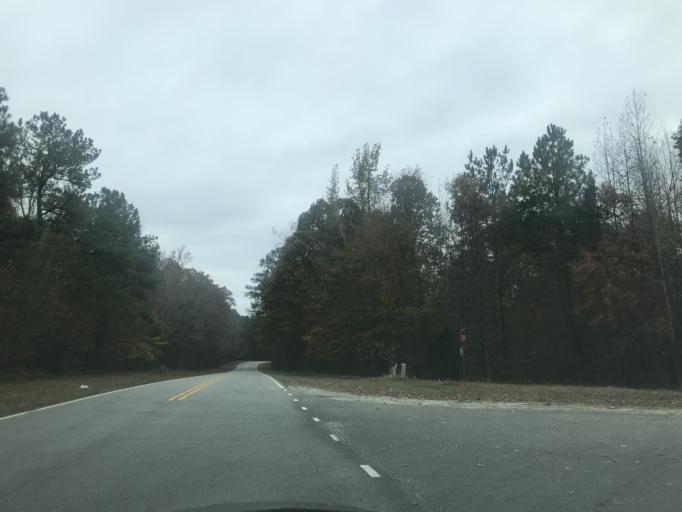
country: US
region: North Carolina
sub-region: Franklin County
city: Youngsville
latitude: 36.0099
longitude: -78.4908
